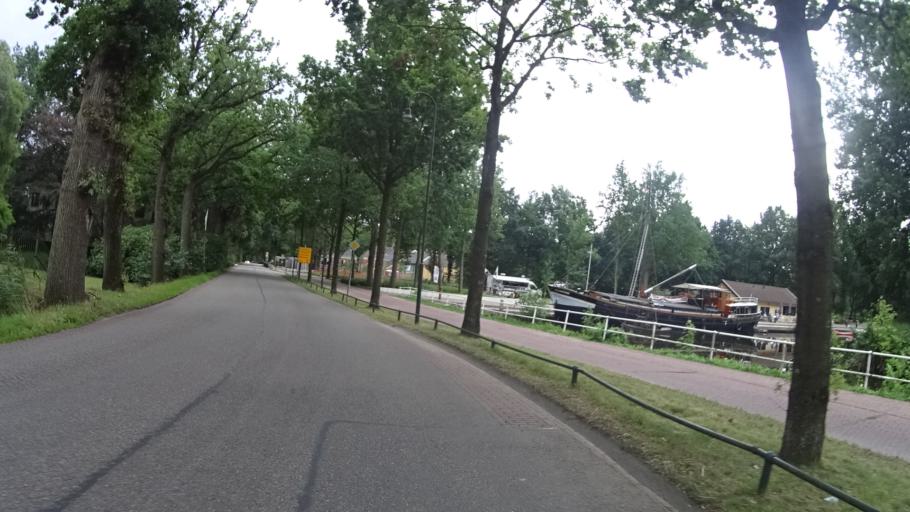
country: NL
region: Groningen
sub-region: Gemeente Slochteren
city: Slochteren
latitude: 53.2183
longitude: 6.8060
